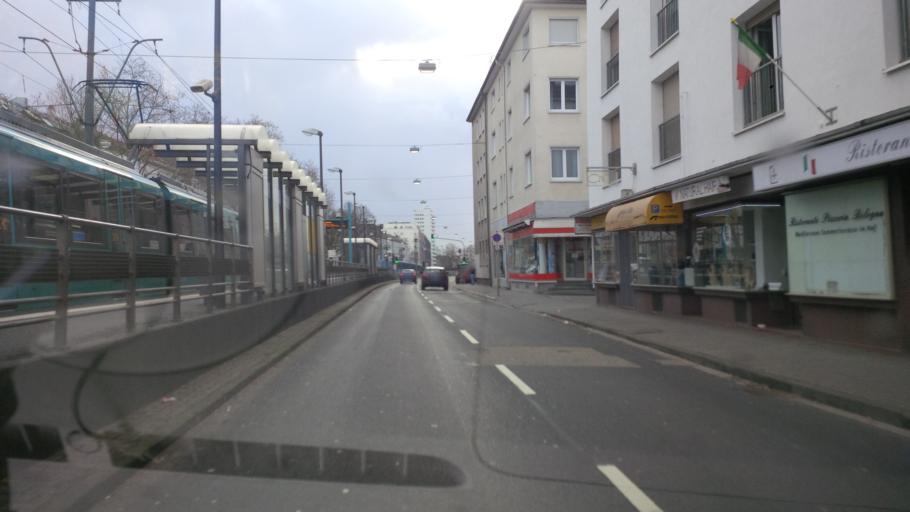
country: DE
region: Hesse
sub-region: Regierungsbezirk Darmstadt
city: Frankfurt am Main
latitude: 50.1373
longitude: 8.6709
